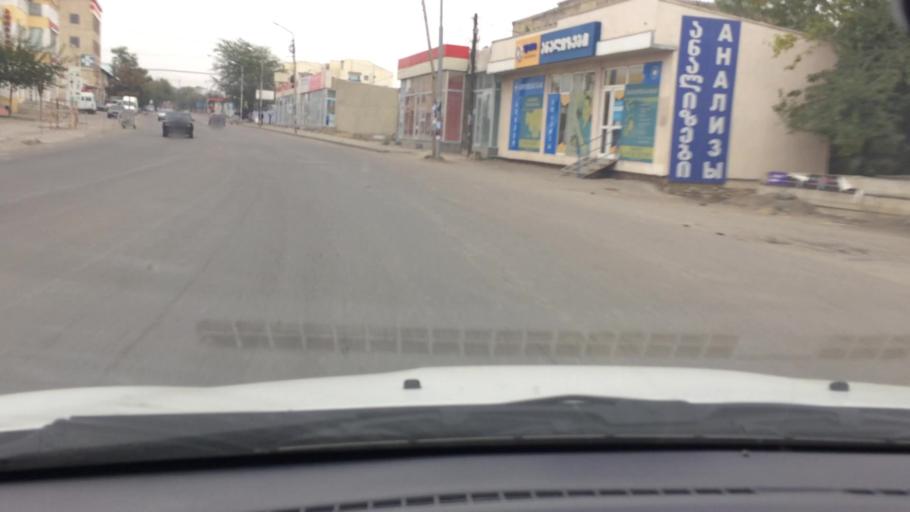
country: GE
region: Kvemo Kartli
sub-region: Marneuli
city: Marneuli
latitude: 41.4838
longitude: 44.7948
